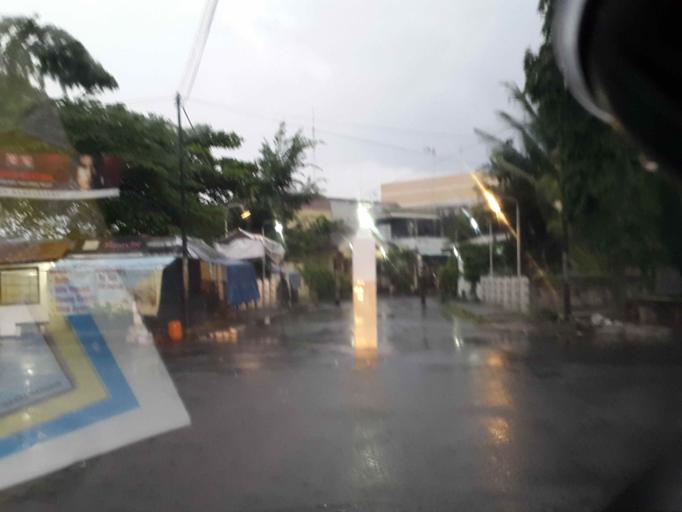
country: ID
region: Central Java
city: Surakarta
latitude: -7.5616
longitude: 110.8217
